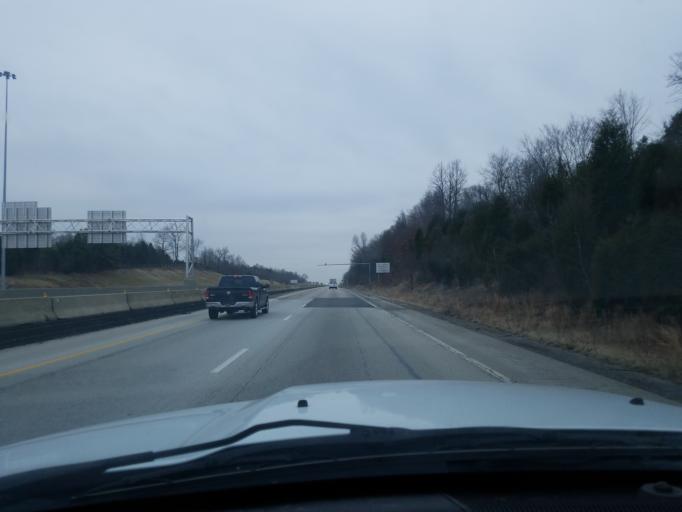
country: US
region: Kentucky
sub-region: Hardin County
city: Elizabethtown
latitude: 37.6667
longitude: -85.8539
